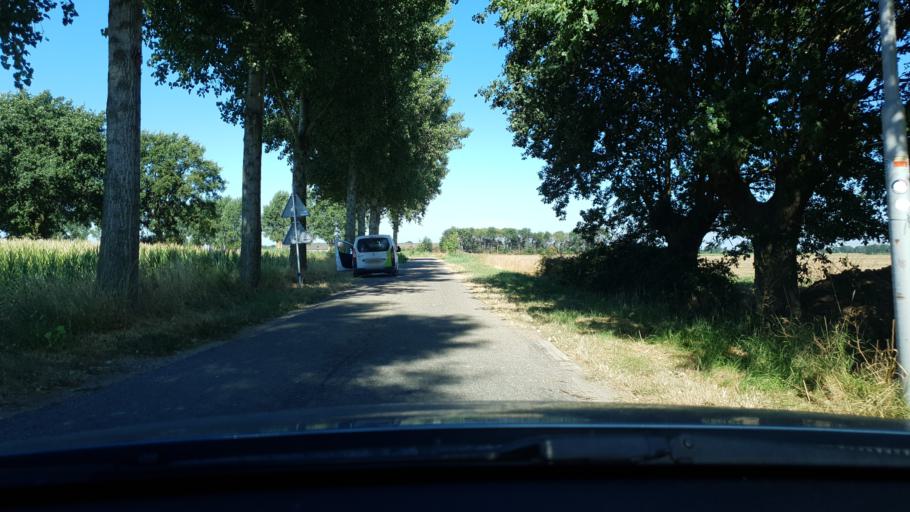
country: NL
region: North Brabant
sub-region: Gemeente Grave
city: Grave
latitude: 51.7761
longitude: 5.7593
